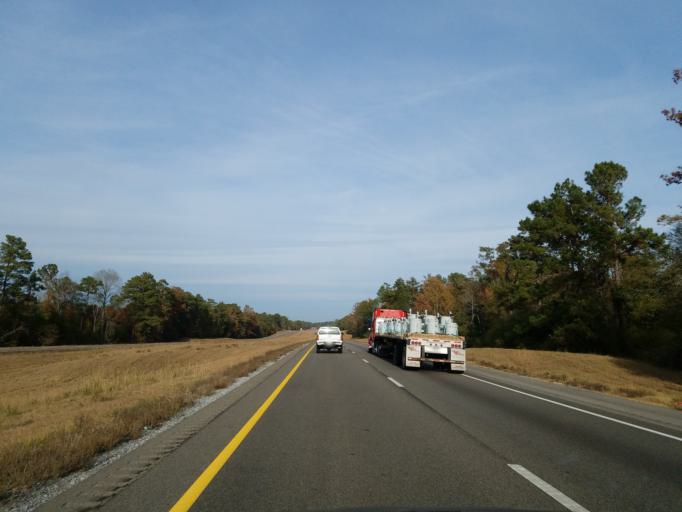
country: US
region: Mississippi
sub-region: Jones County
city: Sharon
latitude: 31.7439
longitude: -89.0822
